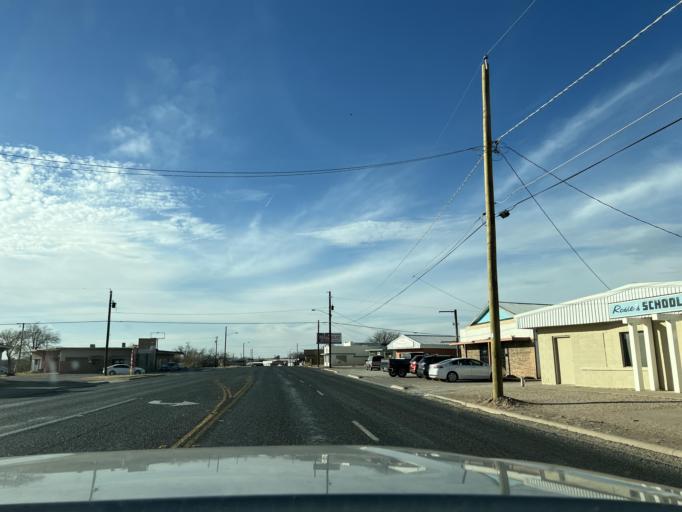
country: US
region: Texas
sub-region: Scurry County
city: Snyder
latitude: 32.7160
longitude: -100.9022
